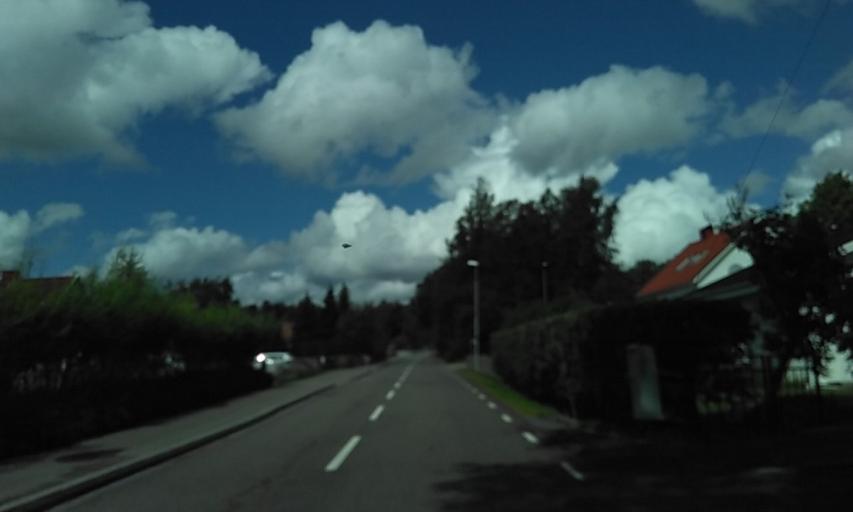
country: SE
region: Vaestra Goetaland
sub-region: Lerums Kommun
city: Grabo
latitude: 57.9163
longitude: 12.3684
